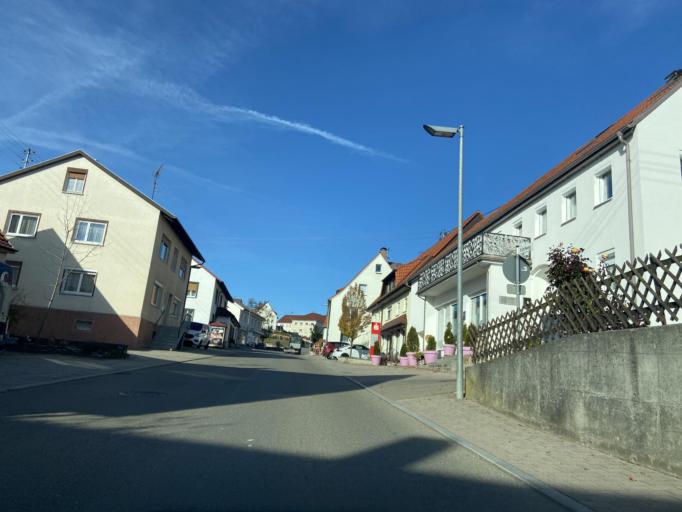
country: DE
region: Baden-Wuerttemberg
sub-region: Tuebingen Region
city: Schwenningen
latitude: 48.1045
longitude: 8.9975
